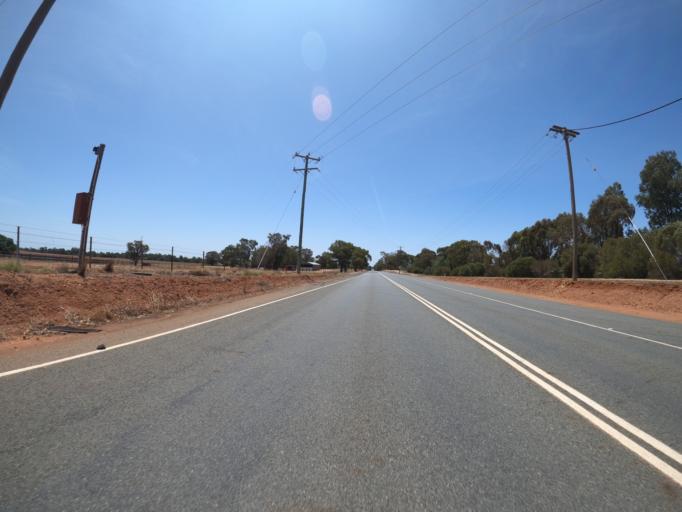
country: AU
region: Victoria
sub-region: Moira
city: Yarrawonga
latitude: -36.0475
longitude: 145.9955
